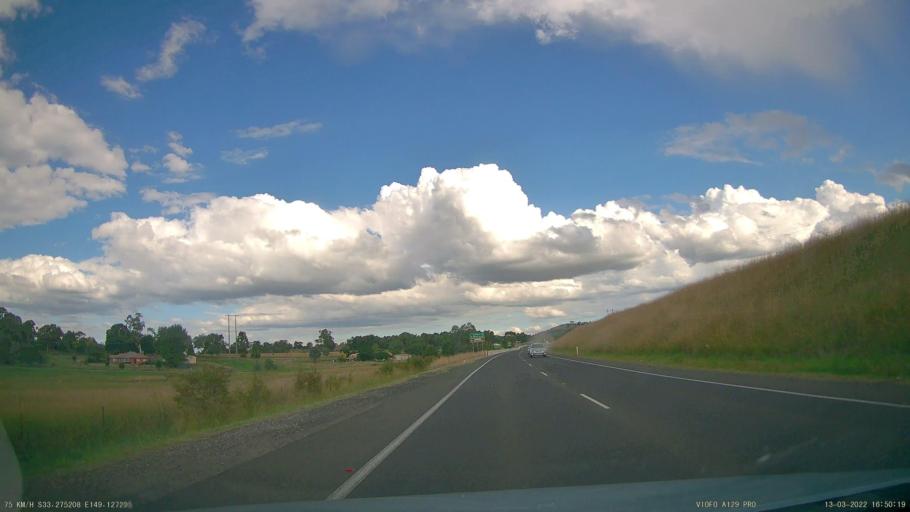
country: AU
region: New South Wales
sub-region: Orange Municipality
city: Orange
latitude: -33.2754
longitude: 149.1275
